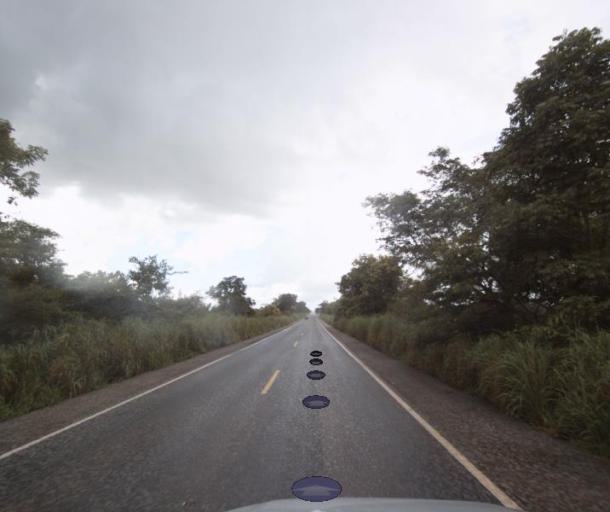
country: BR
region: Goias
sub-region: Porangatu
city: Porangatu
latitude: -13.3342
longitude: -49.1205
